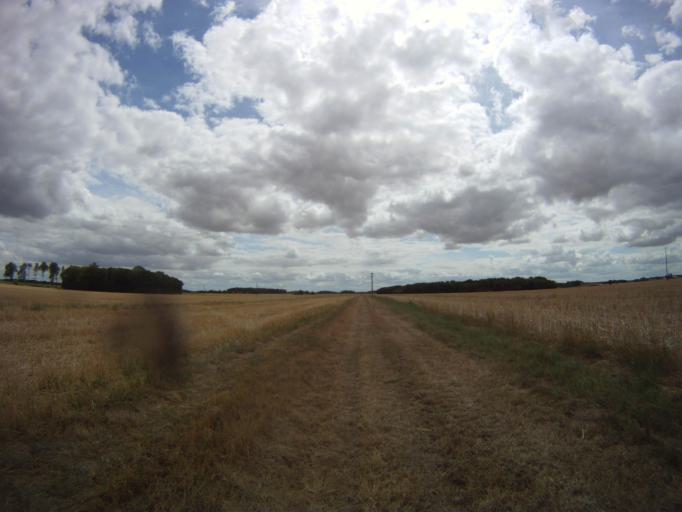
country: FR
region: Centre
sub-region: Departement du Loir-et-Cher
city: Montoire-sur-le-Loir
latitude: 47.6940
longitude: 0.8103
